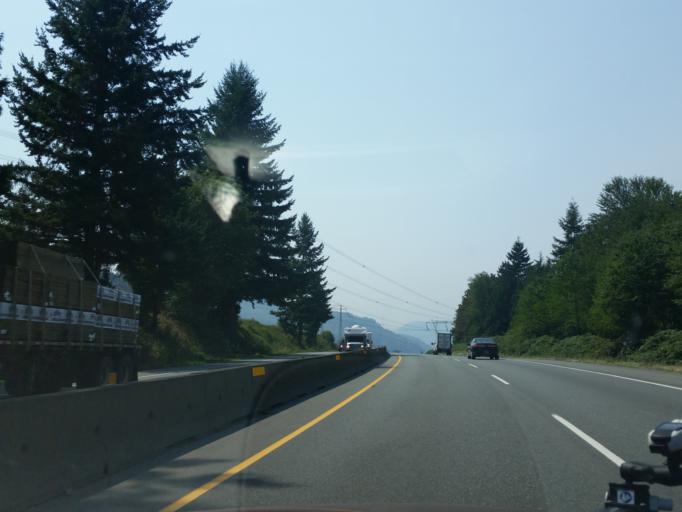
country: CA
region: British Columbia
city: Agassiz
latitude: 49.1600
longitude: -121.8114
